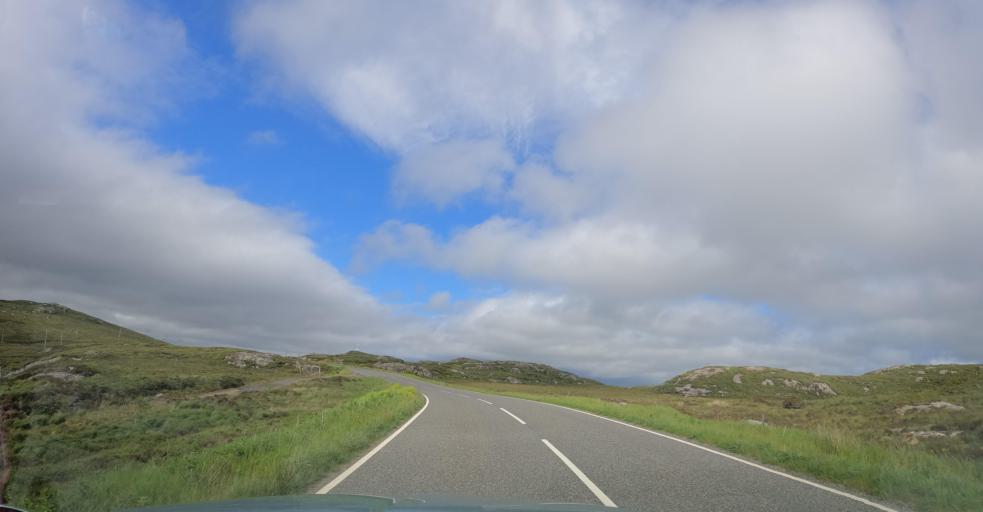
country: GB
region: Scotland
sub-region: Eilean Siar
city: Stornoway
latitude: 58.1241
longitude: -6.5079
